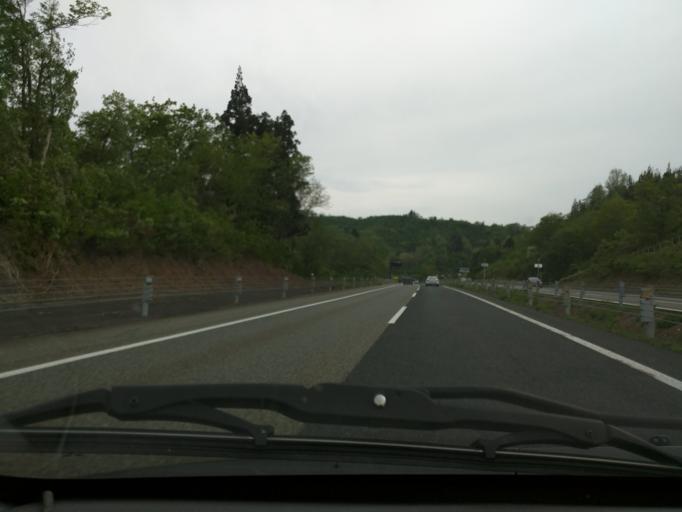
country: JP
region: Niigata
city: Muikamachi
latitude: 37.2012
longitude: 138.9633
